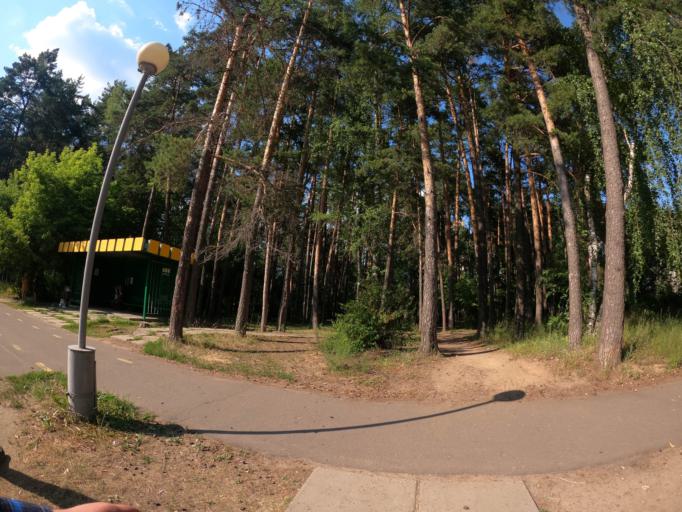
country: RU
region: Moskovskaya
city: Protvino
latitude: 54.8658
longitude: 37.2090
